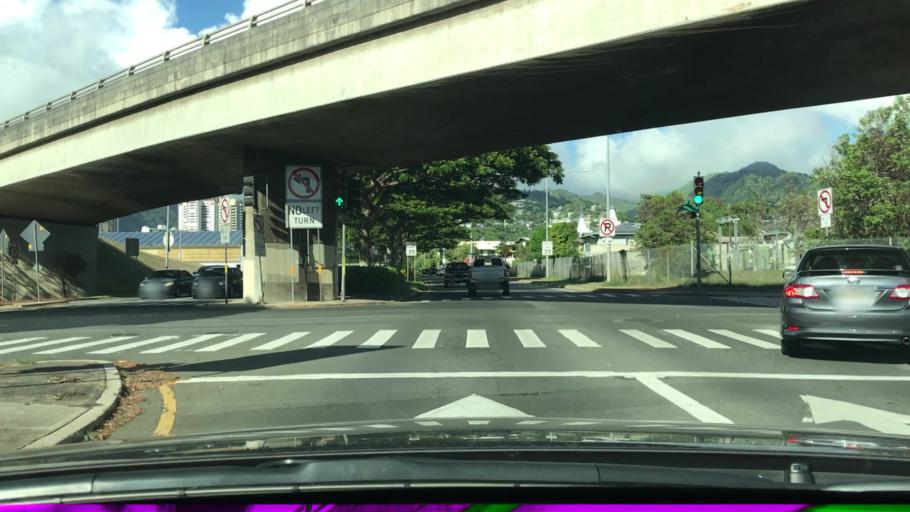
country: US
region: Hawaii
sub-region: Honolulu County
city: Honolulu
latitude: 21.3146
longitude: -157.8544
